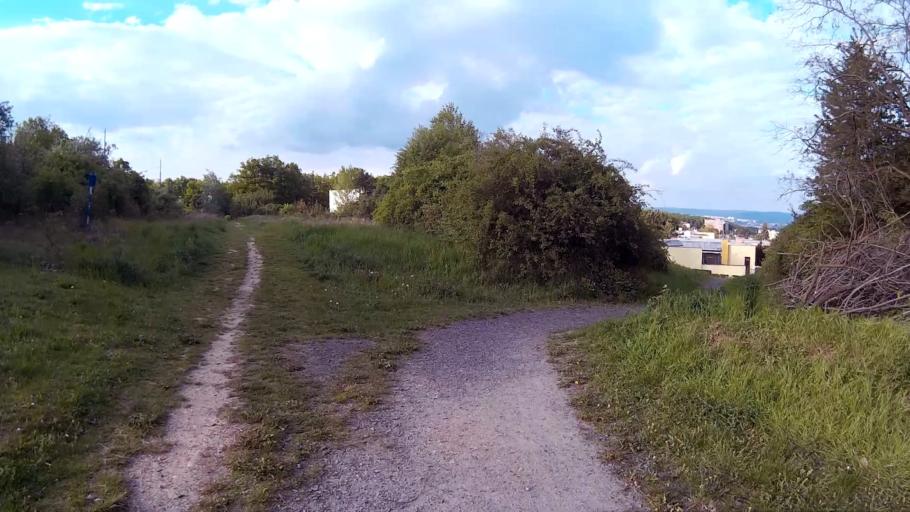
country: CZ
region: South Moravian
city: Troubsko
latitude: 49.1919
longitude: 16.5305
